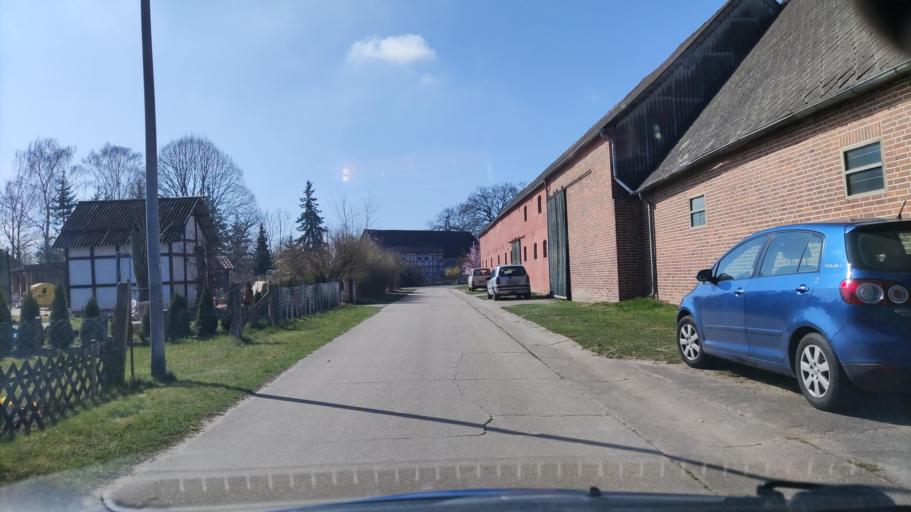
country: DE
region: Lower Saxony
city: Wustrow
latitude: 52.9402
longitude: 11.0956
